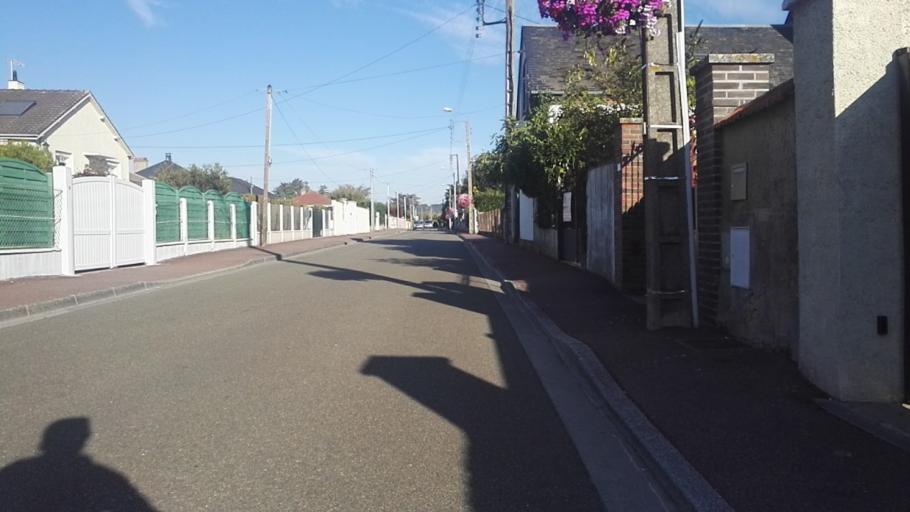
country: FR
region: Haute-Normandie
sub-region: Departement de l'Eure
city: Pacy-sur-Eure
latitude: 49.0197
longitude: 1.3758
